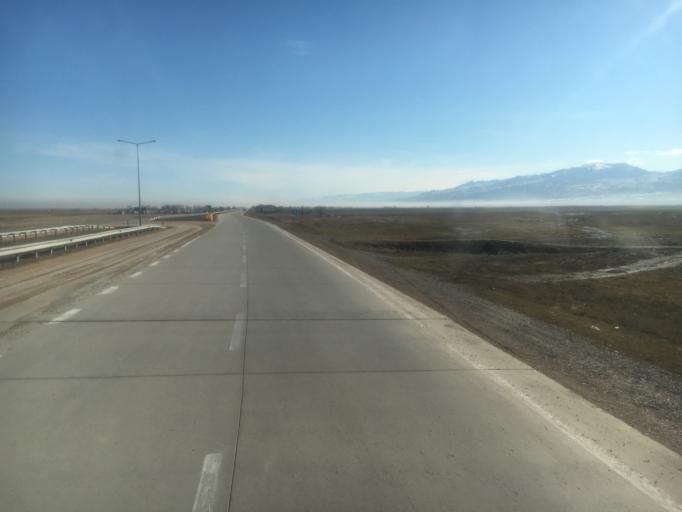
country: KZ
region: Zhambyl
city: Merke
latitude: 42.8885
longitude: 72.9927
